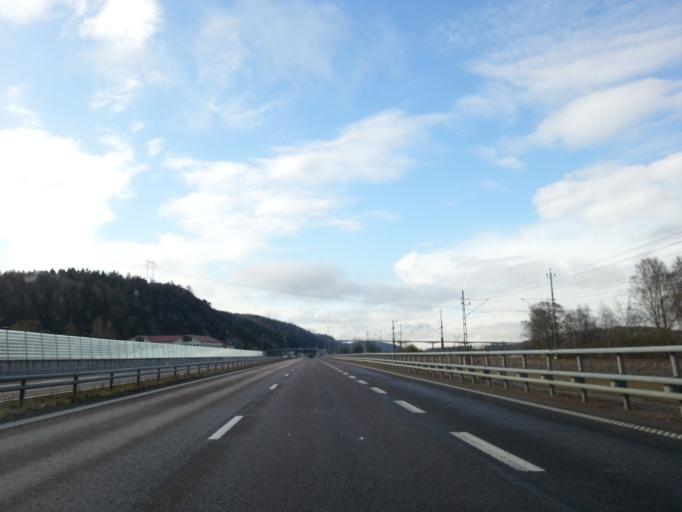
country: SE
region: Vaestra Goetaland
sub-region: Ale Kommun
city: Surte
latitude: 57.8209
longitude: 12.0146
